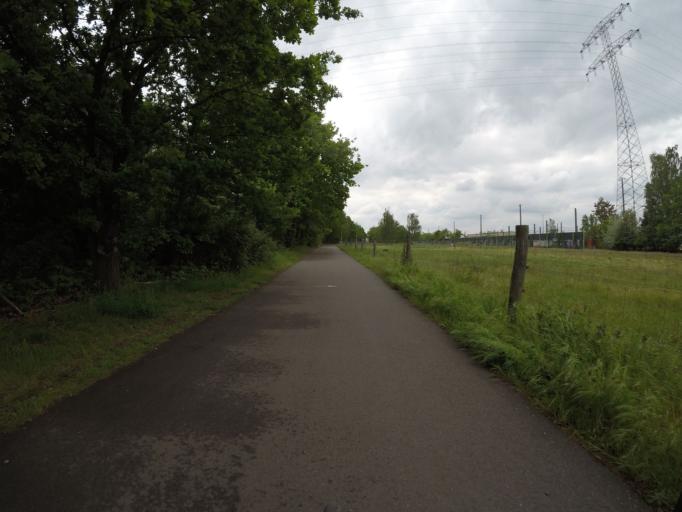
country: DE
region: Berlin
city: Lichtenberg
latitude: 52.5219
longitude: 13.5055
